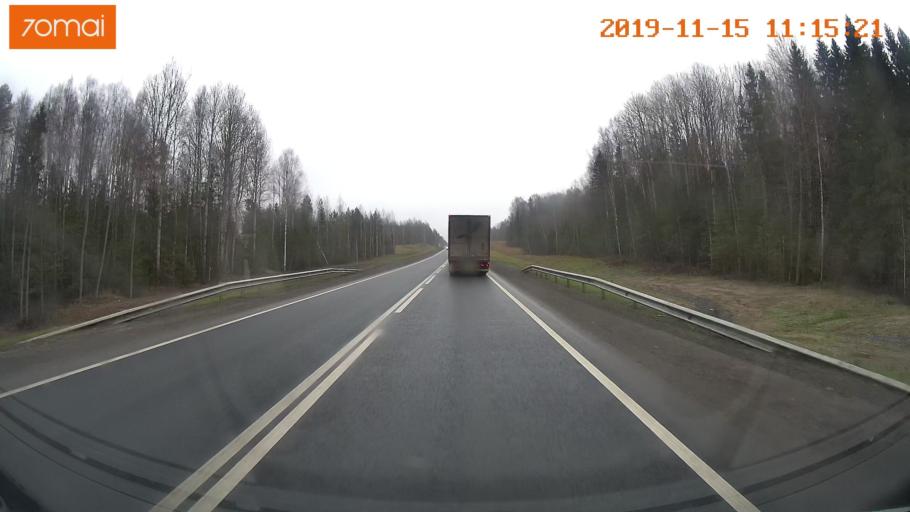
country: RU
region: Vologda
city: Chebsara
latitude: 59.1274
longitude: 39.2075
